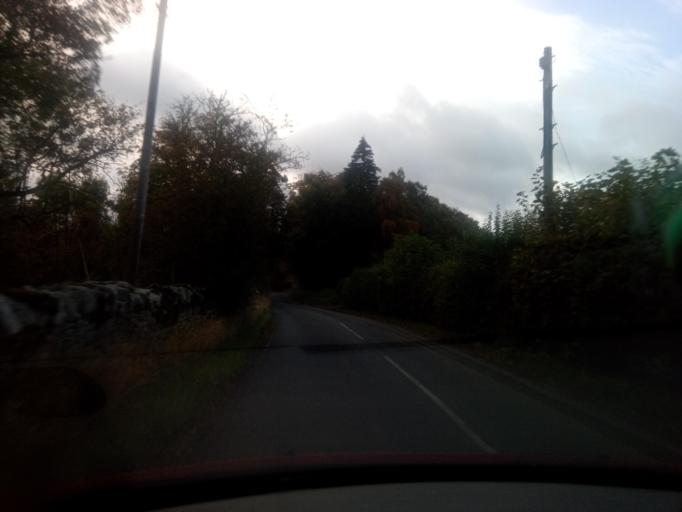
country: GB
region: Scotland
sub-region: The Scottish Borders
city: Jedburgh
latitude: 55.4074
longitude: -2.6549
